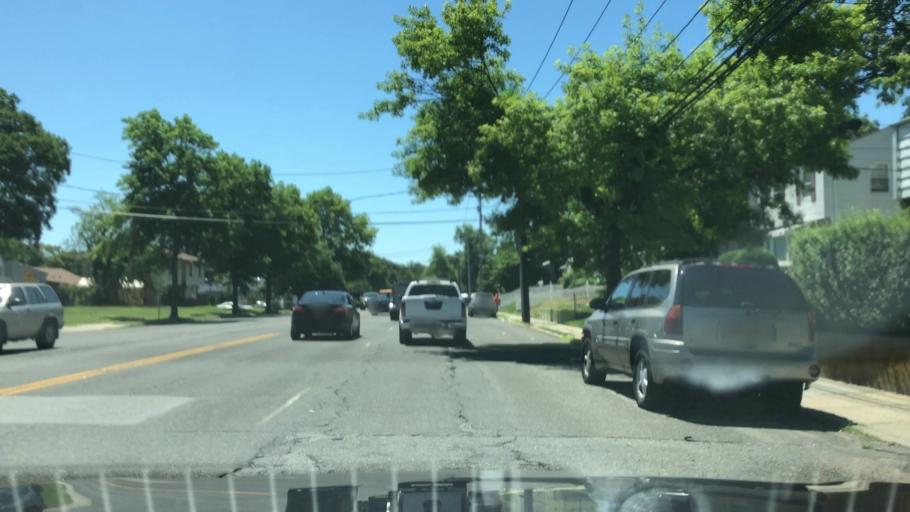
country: US
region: New York
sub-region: Nassau County
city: Hempstead
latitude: 40.7015
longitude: -73.6314
